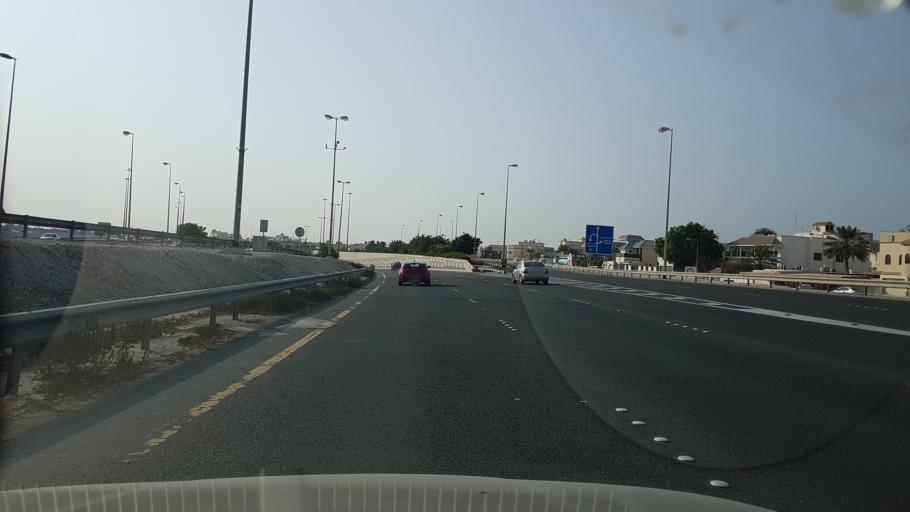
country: BH
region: Central Governorate
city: Madinat Hamad
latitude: 26.1251
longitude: 50.5061
